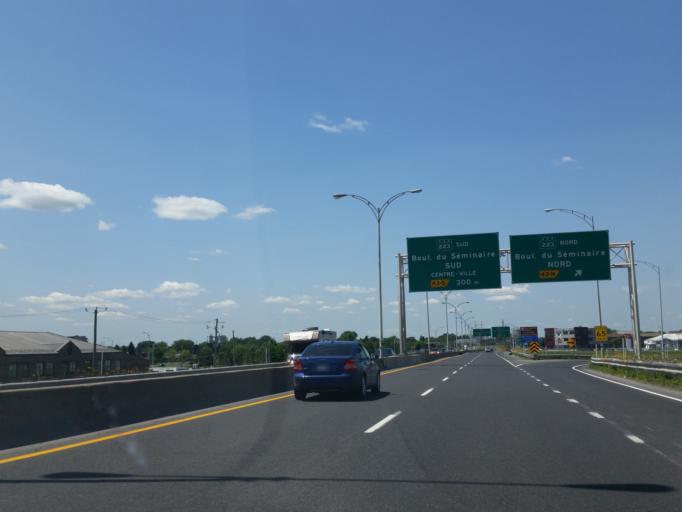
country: CA
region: Quebec
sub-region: Monteregie
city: Saint-Jean-sur-Richelieu
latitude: 45.3269
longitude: -73.2649
